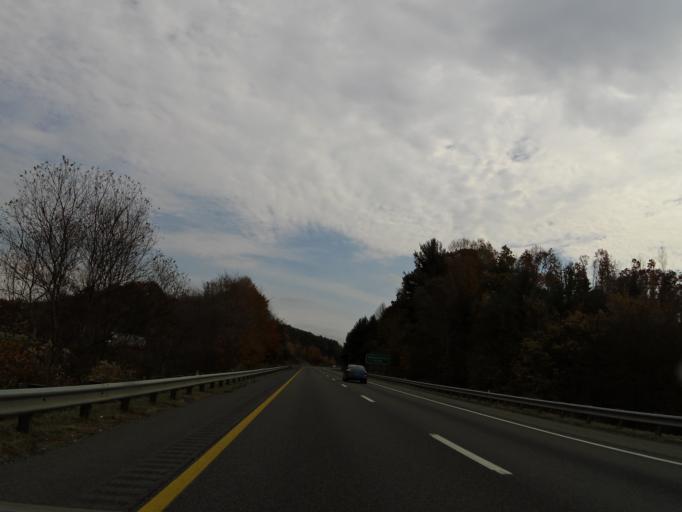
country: US
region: Virginia
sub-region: Carroll County
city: Hillsville
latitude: 36.7544
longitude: -80.7811
